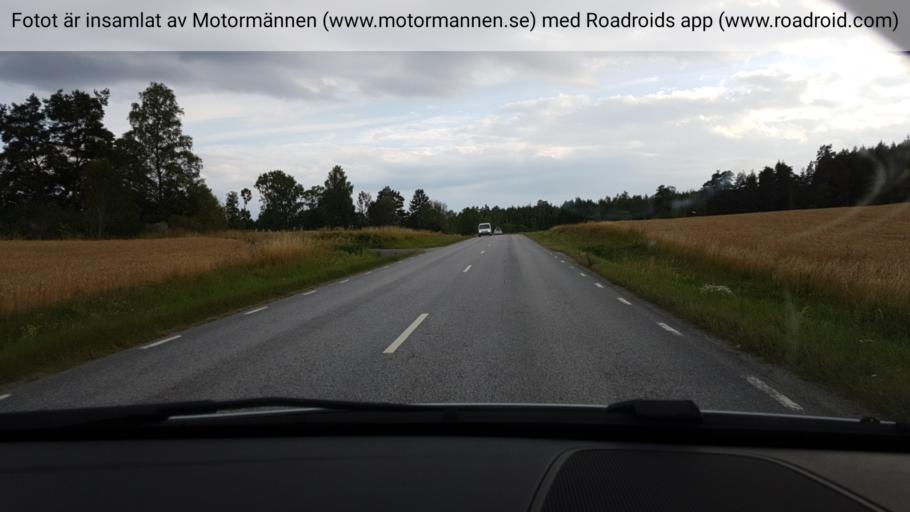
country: SE
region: Uppsala
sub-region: Uppsala Kommun
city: Alsike
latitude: 59.6940
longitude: 17.7164
